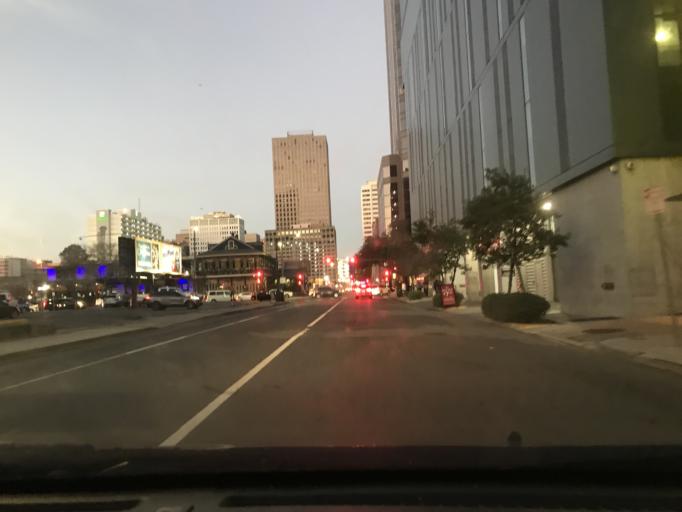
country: US
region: Louisiana
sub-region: Orleans Parish
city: New Orleans
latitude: 29.9496
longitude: -90.0744
